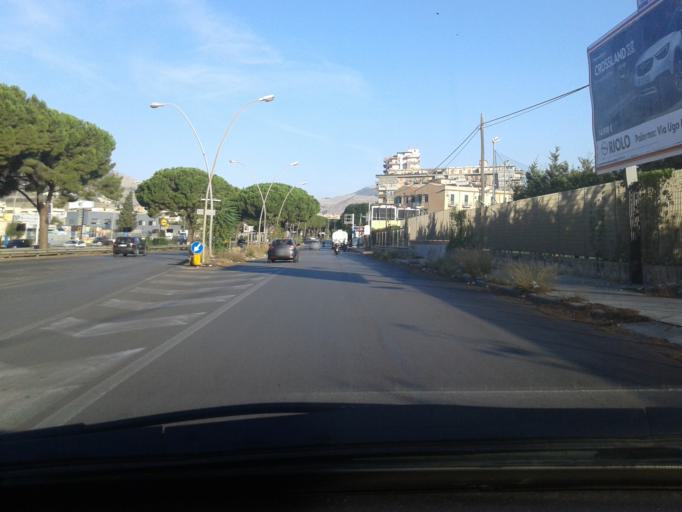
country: IT
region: Sicily
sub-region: Palermo
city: Palermo
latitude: 38.0956
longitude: 13.3372
